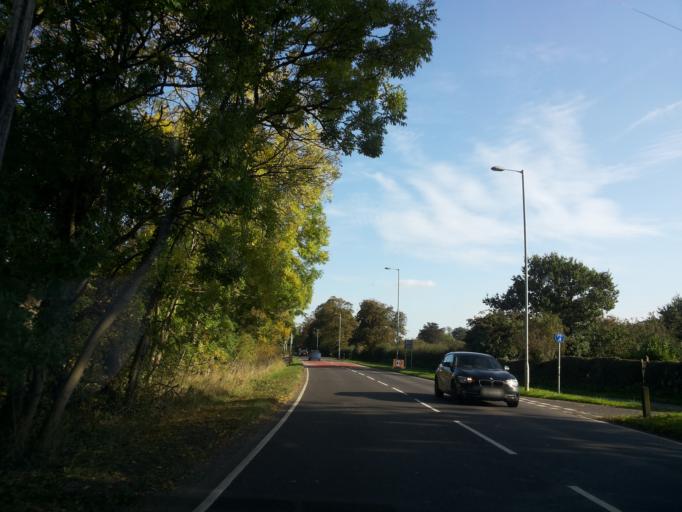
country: GB
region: England
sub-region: East Riding of Yorkshire
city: Snaith
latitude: 53.6892
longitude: -1.0193
